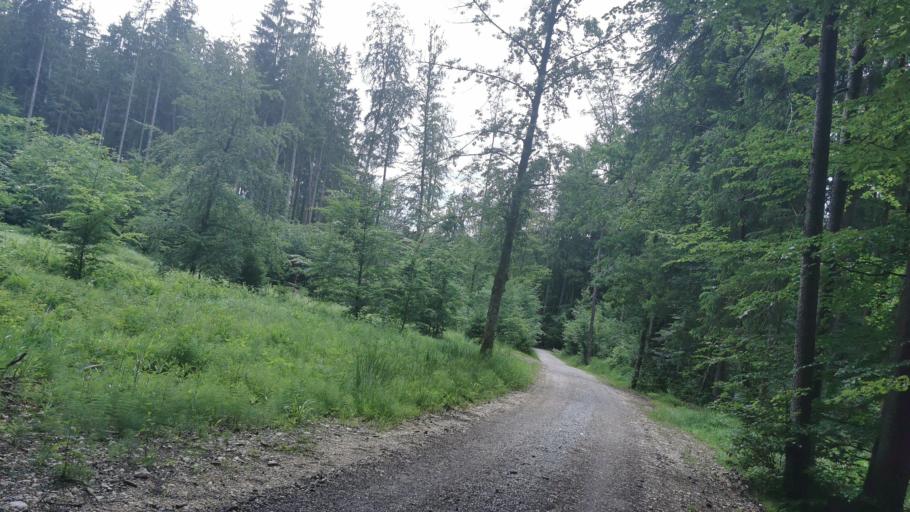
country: AT
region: Salzburg
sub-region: Politischer Bezirk Salzburg-Umgebung
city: Grodig
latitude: 47.7492
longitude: 12.9751
